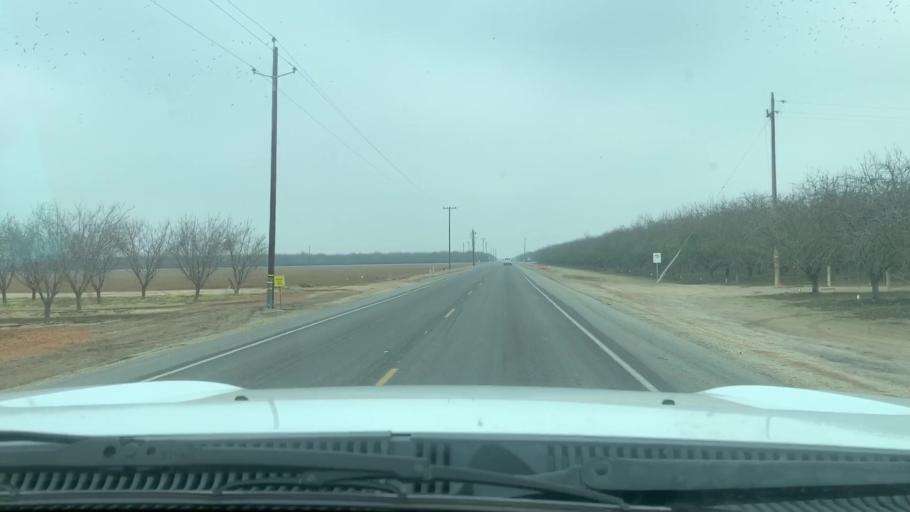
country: US
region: California
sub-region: Kern County
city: Wasco
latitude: 35.5003
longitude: -119.4083
